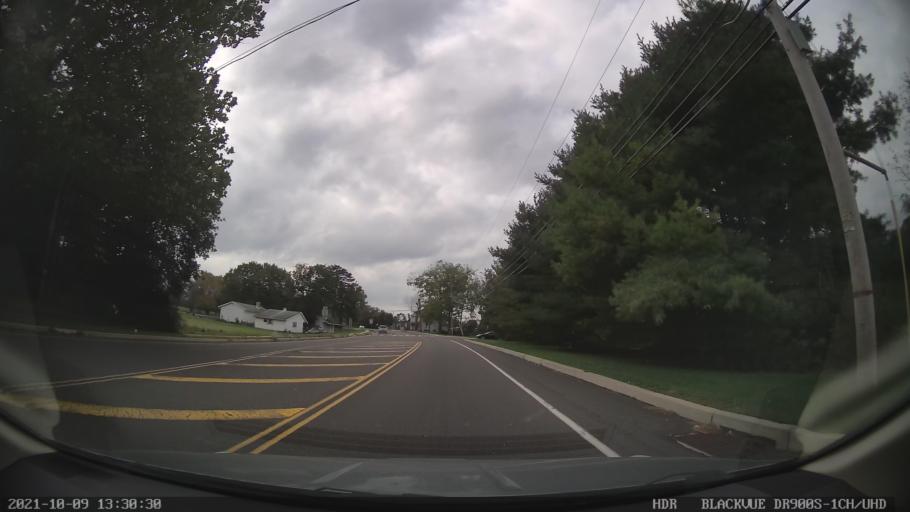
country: US
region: Pennsylvania
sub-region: Lehigh County
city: Trexlertown
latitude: 40.5323
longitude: -75.6058
